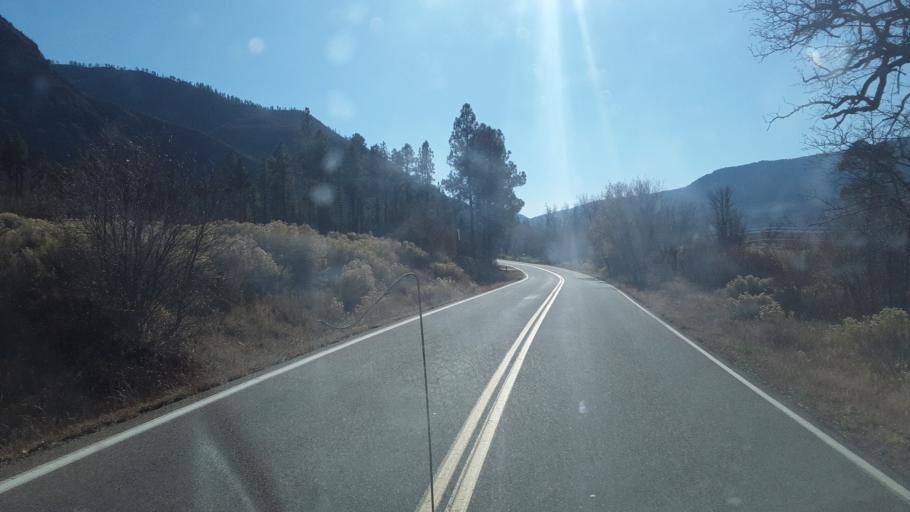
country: US
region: Colorado
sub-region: La Plata County
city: Durango
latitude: 37.4058
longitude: -107.8146
